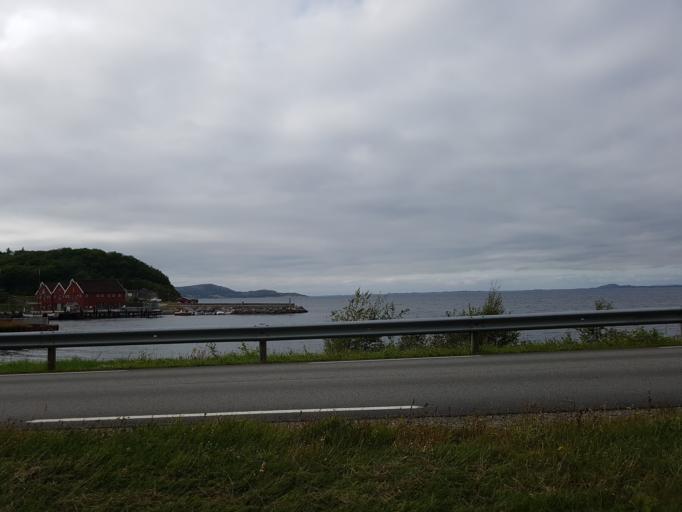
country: NO
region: Sor-Trondelag
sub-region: Agdenes
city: Lensvik
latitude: 63.6336
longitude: 9.8310
